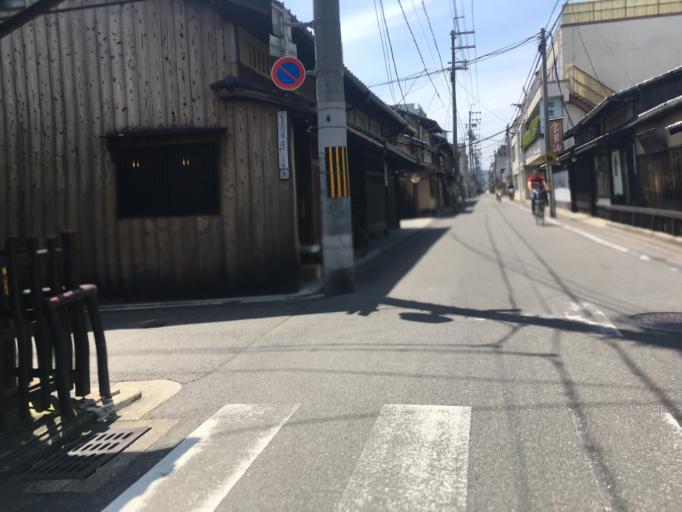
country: JP
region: Kyoto
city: Kyoto
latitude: 35.0201
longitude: 135.7462
